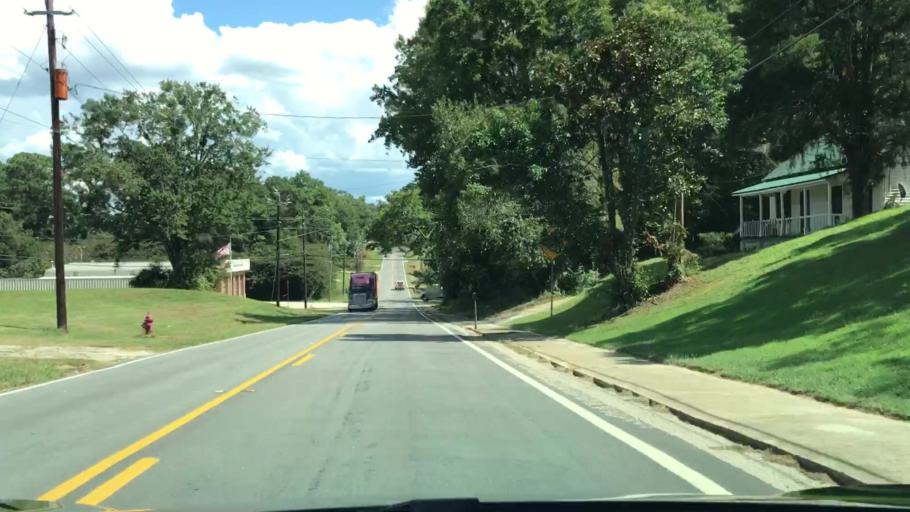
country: US
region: Georgia
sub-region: Greene County
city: Greensboro
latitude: 33.5744
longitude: -83.1765
